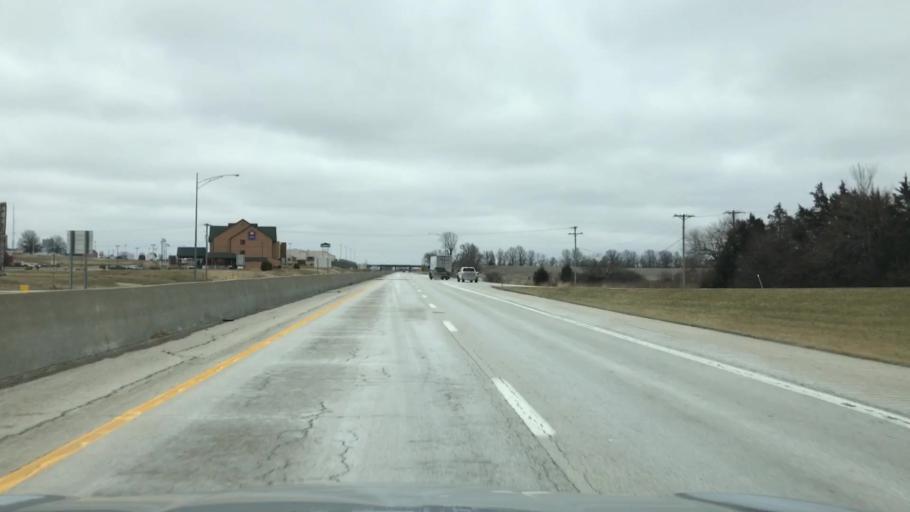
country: US
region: Missouri
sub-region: Livingston County
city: Chillicothe
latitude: 39.7731
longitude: -93.5511
